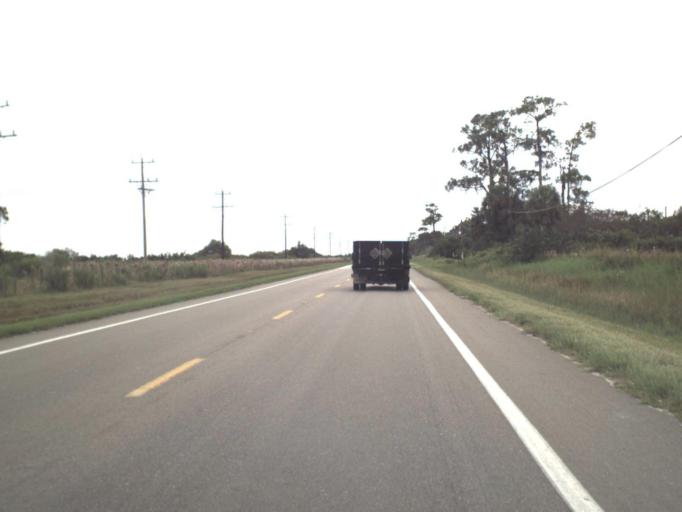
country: US
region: Florida
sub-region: Lee County
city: Fort Myers Shores
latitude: 26.7741
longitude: -81.7608
